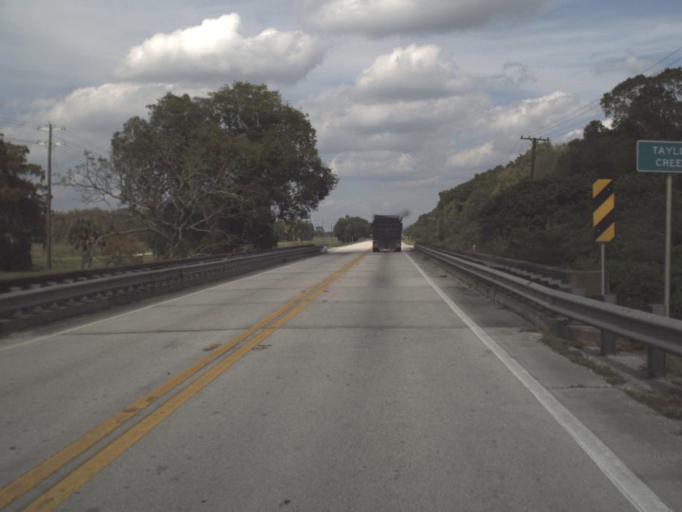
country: US
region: Florida
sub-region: Okeechobee County
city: Cypress Quarters
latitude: 27.2957
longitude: -80.8275
